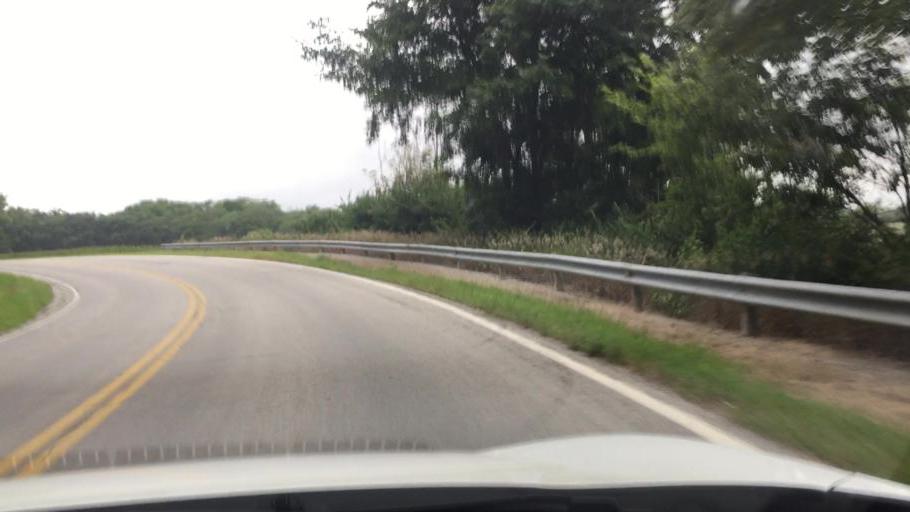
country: US
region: Ohio
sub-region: Clark County
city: Northridge
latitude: 39.9876
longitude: -83.6672
